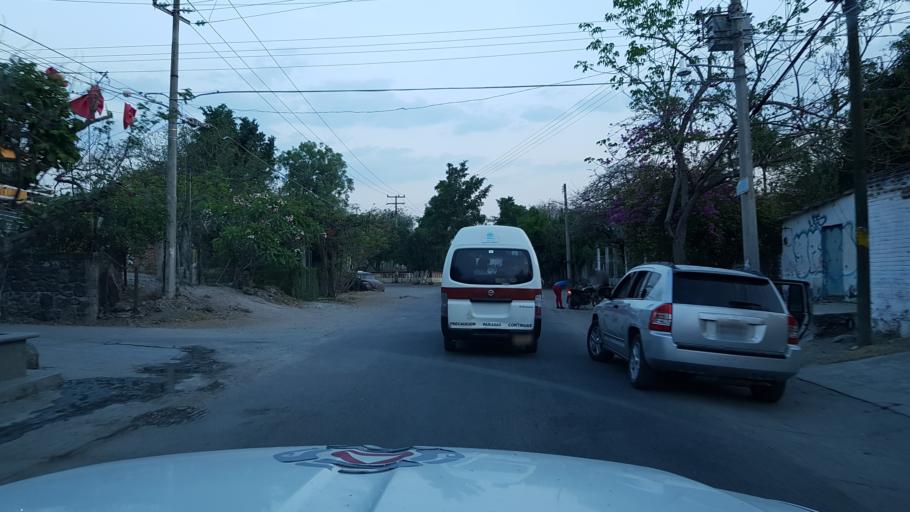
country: MX
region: Morelos
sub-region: Tlaltizapan de Zapata
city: Colonia Palo Prieto (Chipitongo)
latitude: 18.7008
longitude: -99.1059
